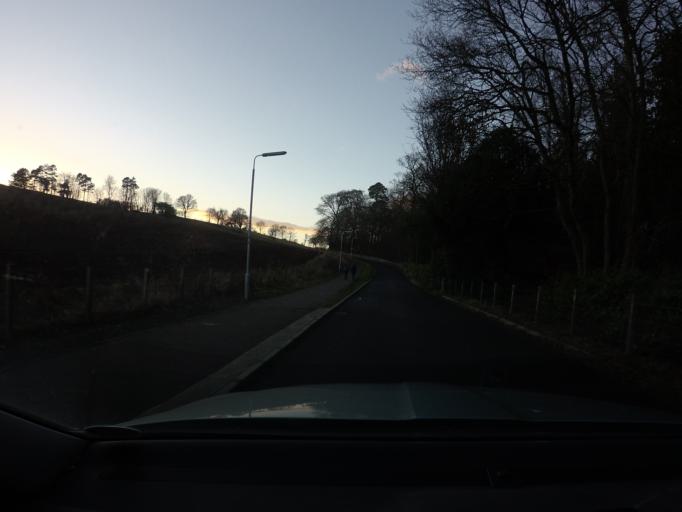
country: GB
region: Scotland
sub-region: Fife
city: Newport-On-Tay
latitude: 56.4328
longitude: -2.9391
